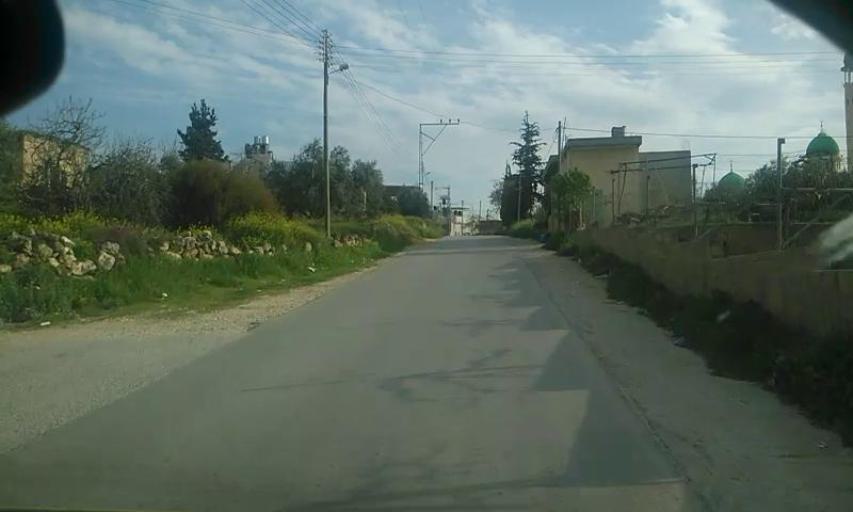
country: PS
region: West Bank
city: Nuba
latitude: 31.6112
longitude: 35.0342
